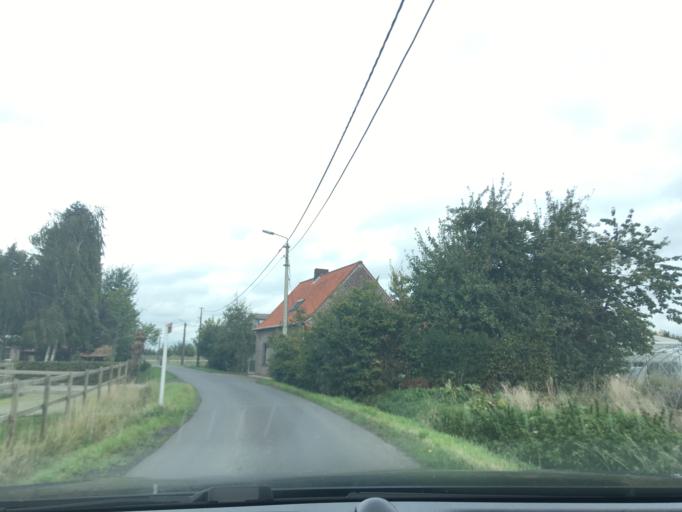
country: BE
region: Flanders
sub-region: Provincie West-Vlaanderen
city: Moorslede
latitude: 50.9064
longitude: 3.0915
